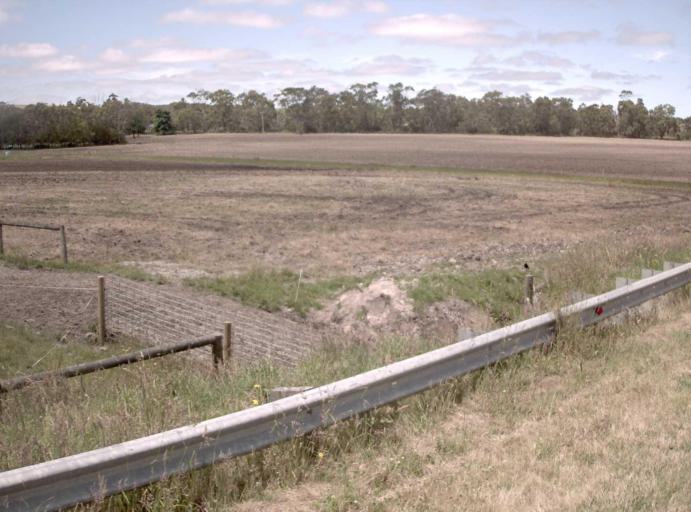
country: AU
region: Victoria
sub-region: Bass Coast
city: North Wonthaggi
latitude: -38.6544
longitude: 146.0196
